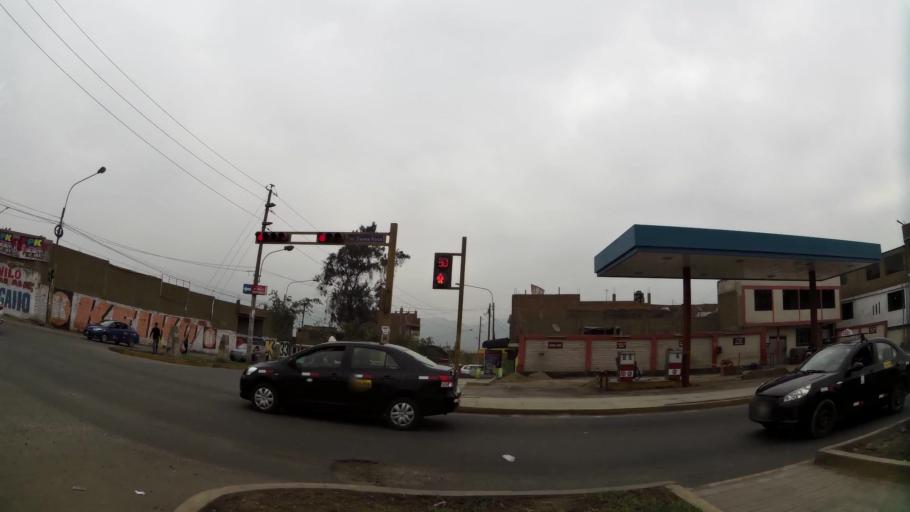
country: PE
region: Lima
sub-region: Lima
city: Independencia
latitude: -11.9787
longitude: -76.9918
